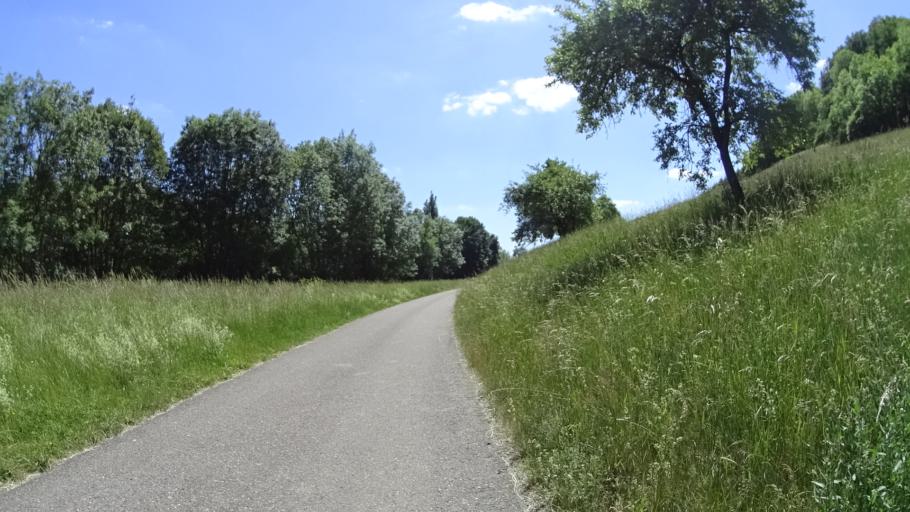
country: DE
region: Bavaria
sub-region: Regierungsbezirk Mittelfranken
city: Adelshofen
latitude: 49.4388
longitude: 10.1363
